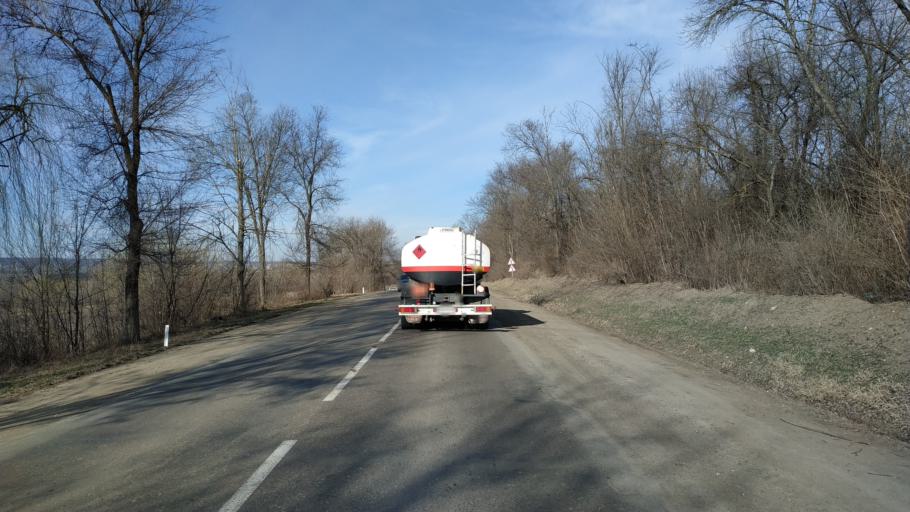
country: MD
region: Laloveni
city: Ialoveni
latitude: 46.9554
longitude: 28.7527
